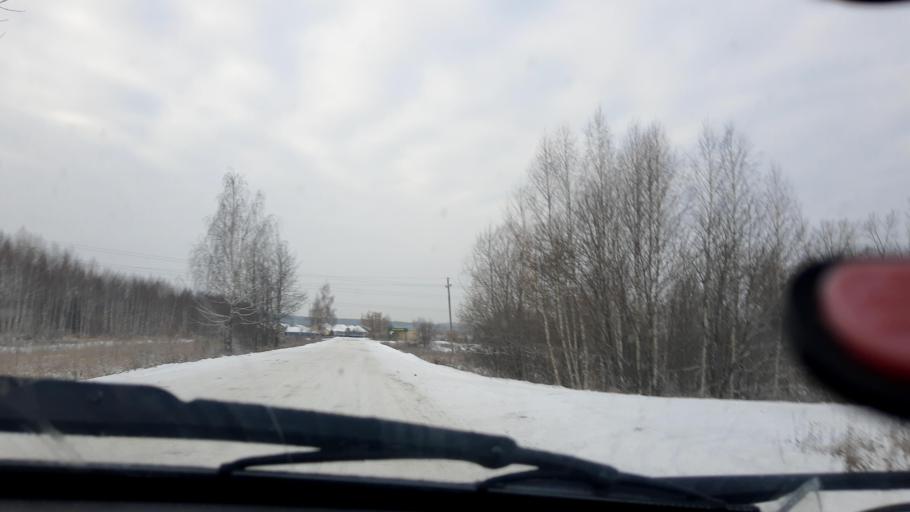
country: RU
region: Bashkortostan
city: Iglino
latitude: 54.7477
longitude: 56.2809
